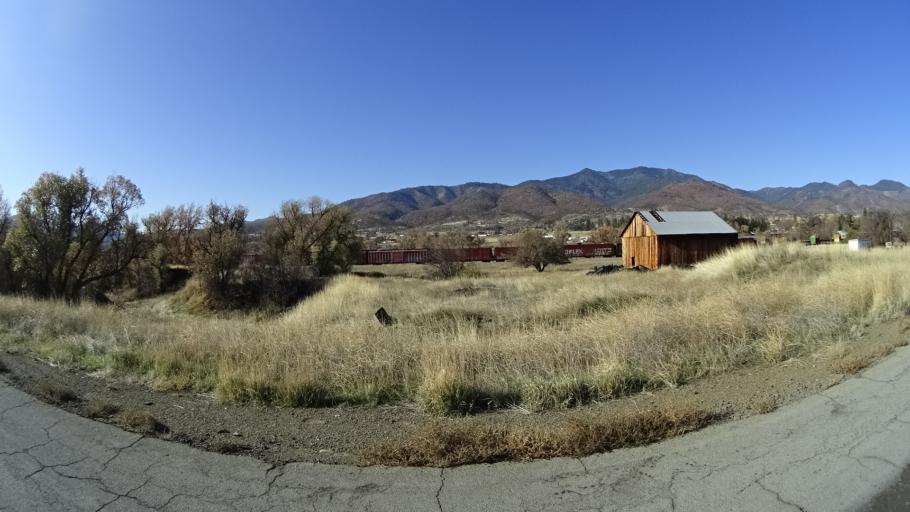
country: US
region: California
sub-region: Siskiyou County
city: Montague
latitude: 41.9074
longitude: -122.5505
